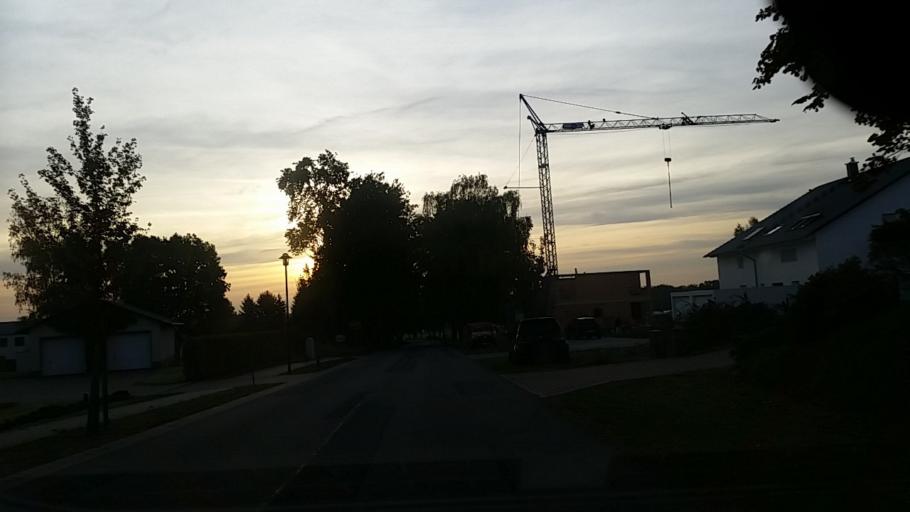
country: DE
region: Lower Saxony
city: Barwedel
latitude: 52.5203
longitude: 10.7865
